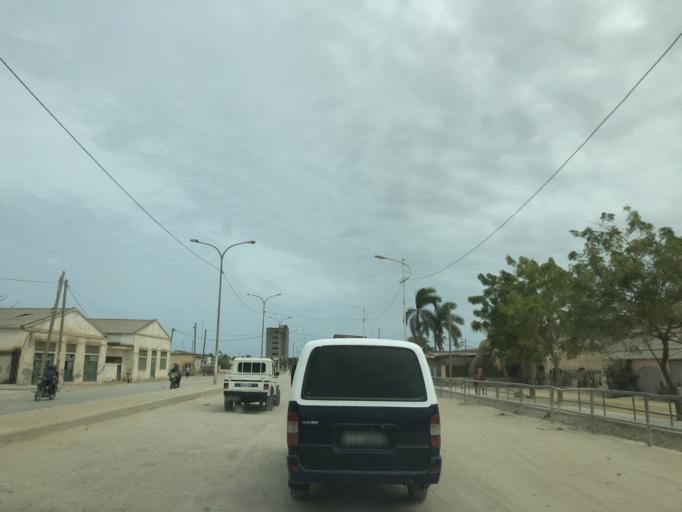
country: AO
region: Cuanza Sul
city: Sumbe
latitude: -11.2100
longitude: 13.8457
